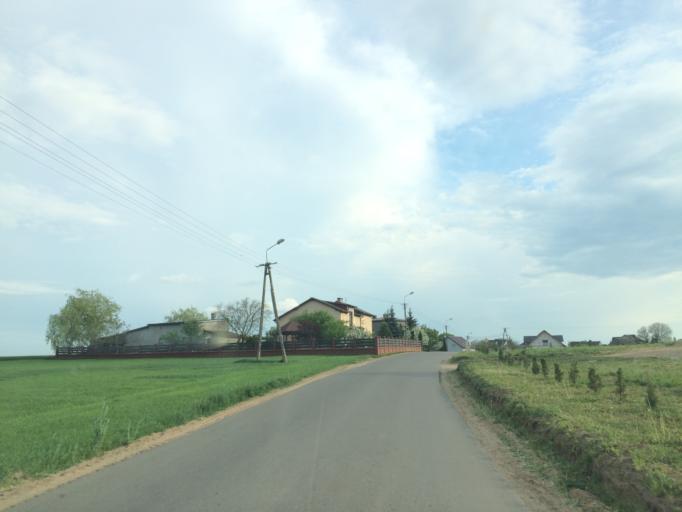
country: PL
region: Kujawsko-Pomorskie
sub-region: Powiat brodnicki
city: Brzozie
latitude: 53.3605
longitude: 19.7104
